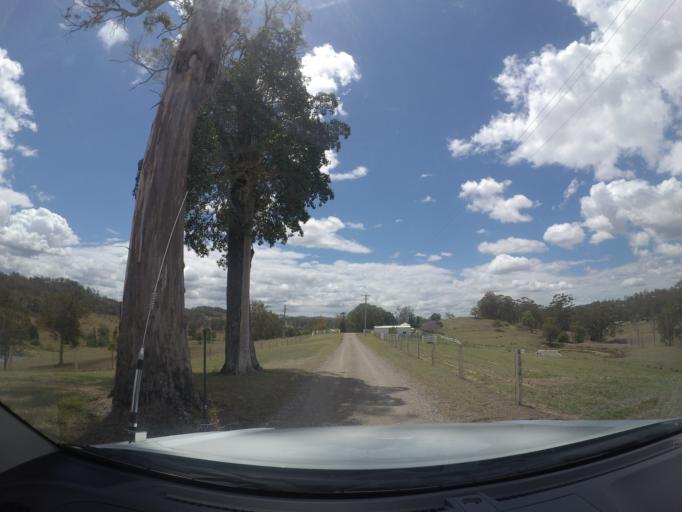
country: AU
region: Queensland
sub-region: Logan
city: Cedar Vale
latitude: -27.9066
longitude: 153.0572
